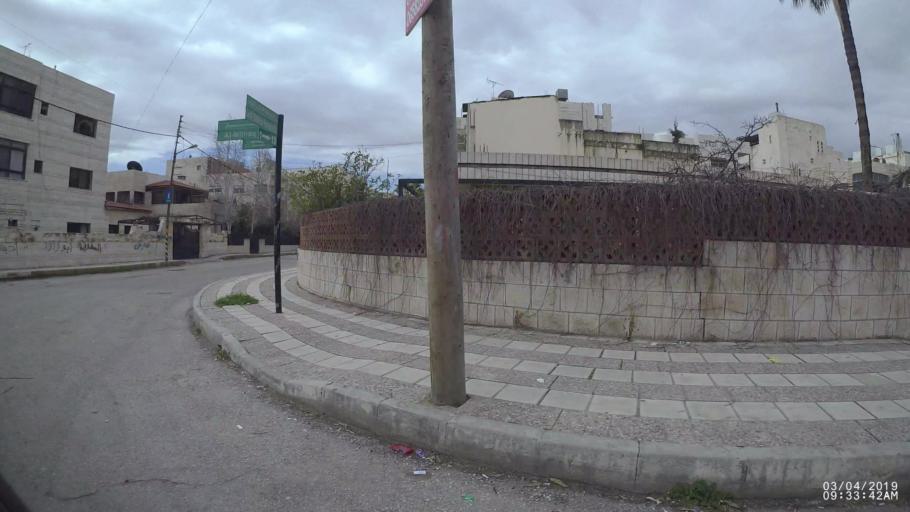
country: JO
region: Amman
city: Wadi as Sir
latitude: 31.9503
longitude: 35.8379
